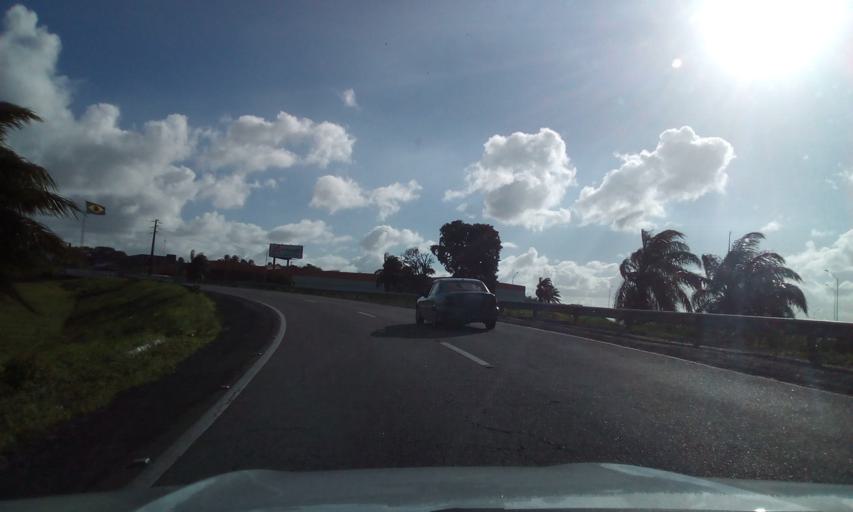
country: BR
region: Paraiba
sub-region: Bayeux
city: Bayeux
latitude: -7.1236
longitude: -34.9454
